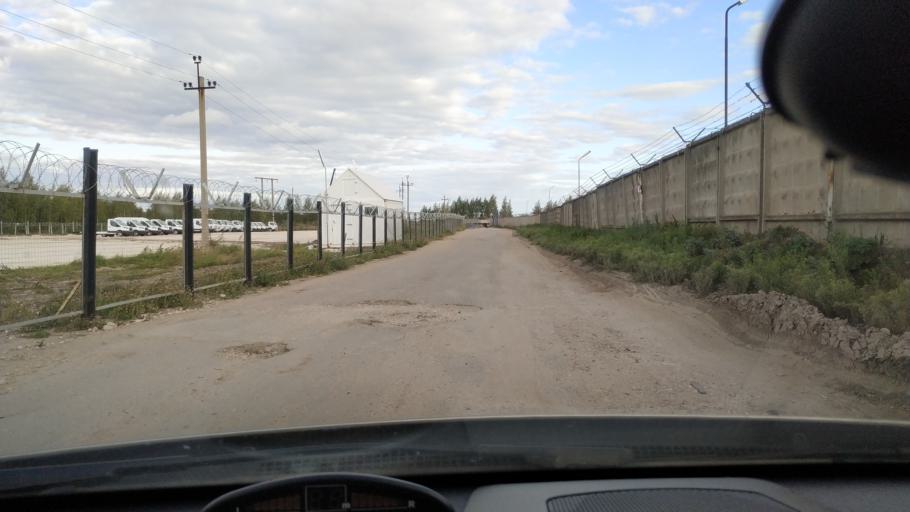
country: RU
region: Rjazan
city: Polyany
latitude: 54.5778
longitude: 39.8412
